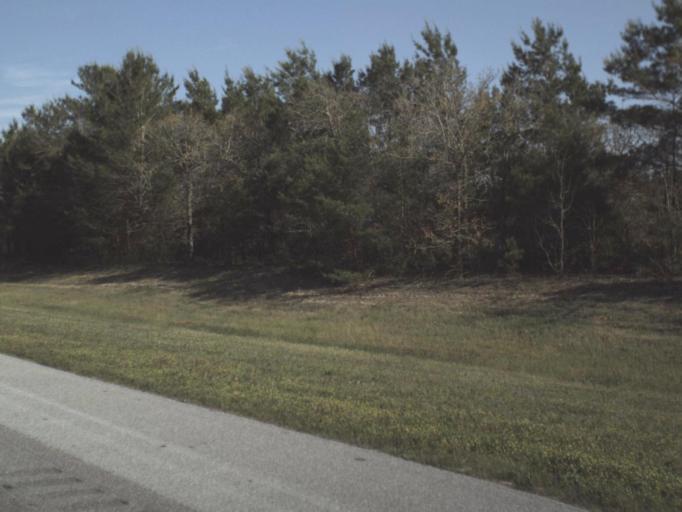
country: US
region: Florida
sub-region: Okaloosa County
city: Crestview
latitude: 30.7175
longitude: -86.4483
